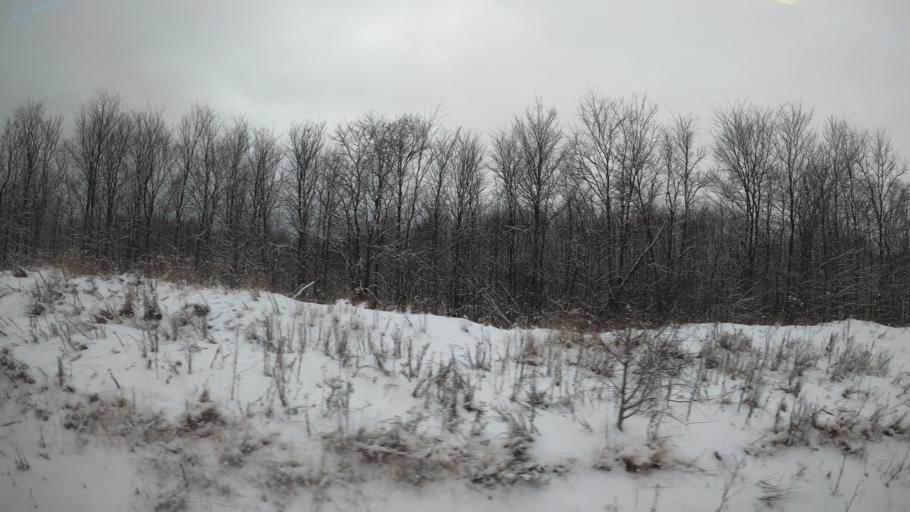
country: RU
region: Jaroslavl
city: Pereslavl'-Zalesskiy
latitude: 56.6907
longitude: 38.9155
